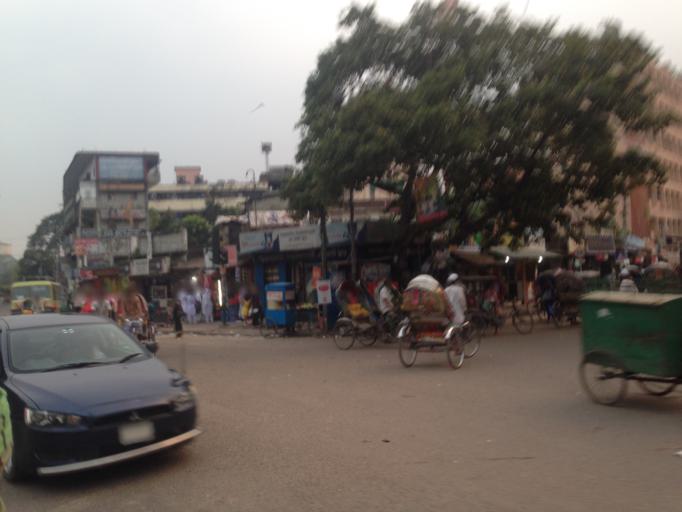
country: BD
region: Dhaka
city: Paltan
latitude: 23.7367
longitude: 90.4233
